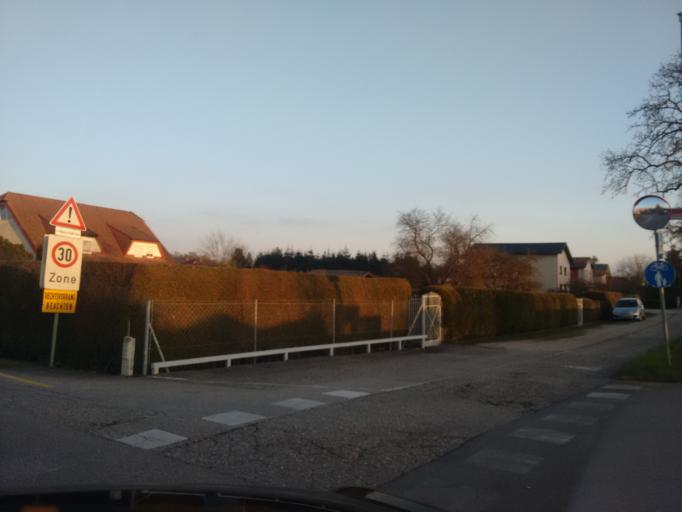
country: AT
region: Upper Austria
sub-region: Wels Stadt
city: Wels
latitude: 48.1698
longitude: 13.9964
